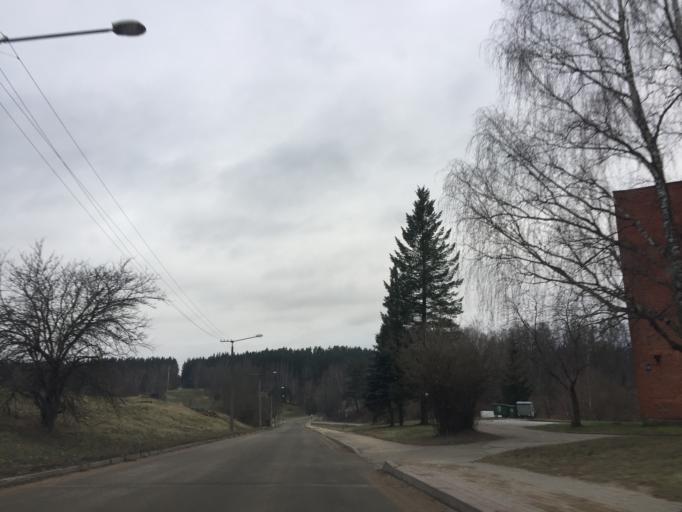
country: LV
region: Cesu Rajons
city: Cesis
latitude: 57.3217
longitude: 25.2614
